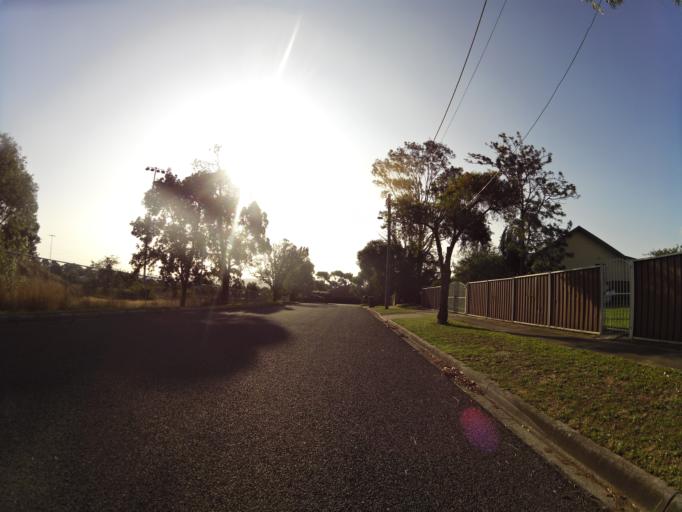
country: AU
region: Victoria
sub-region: Latrobe
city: Morwell
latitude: -38.2390
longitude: 146.3897
